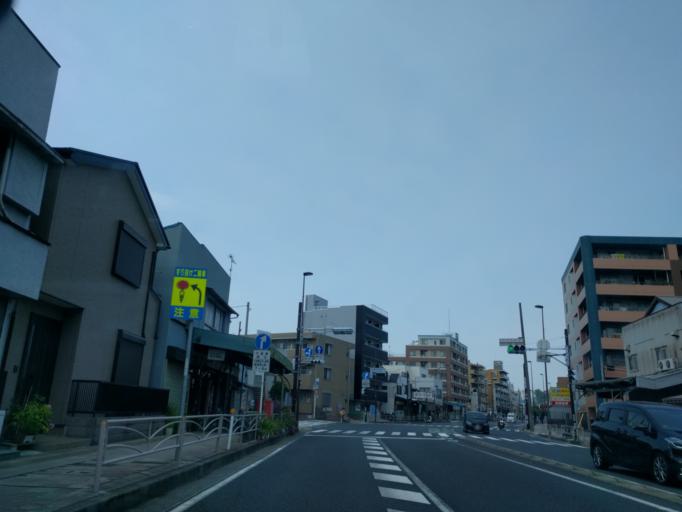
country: JP
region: Kanagawa
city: Yokohama
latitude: 35.4115
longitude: 139.6227
